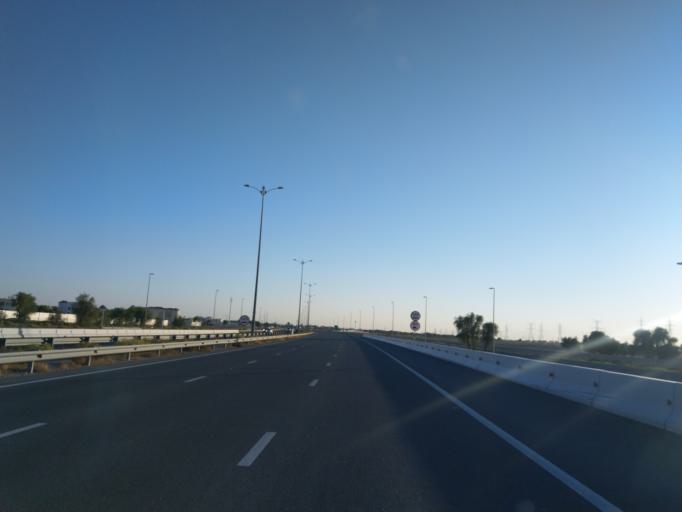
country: OM
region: Al Buraimi
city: Al Buraymi
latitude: 24.2973
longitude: 55.7391
